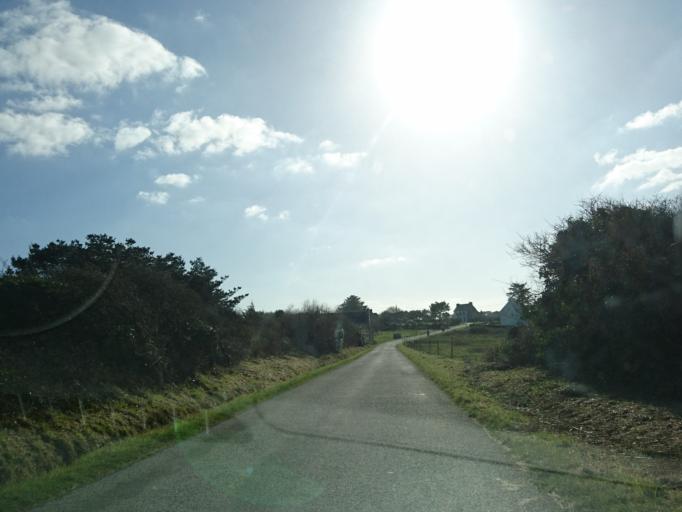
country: FR
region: Brittany
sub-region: Departement du Finistere
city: Roscanvel
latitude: 48.3265
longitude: -4.5694
